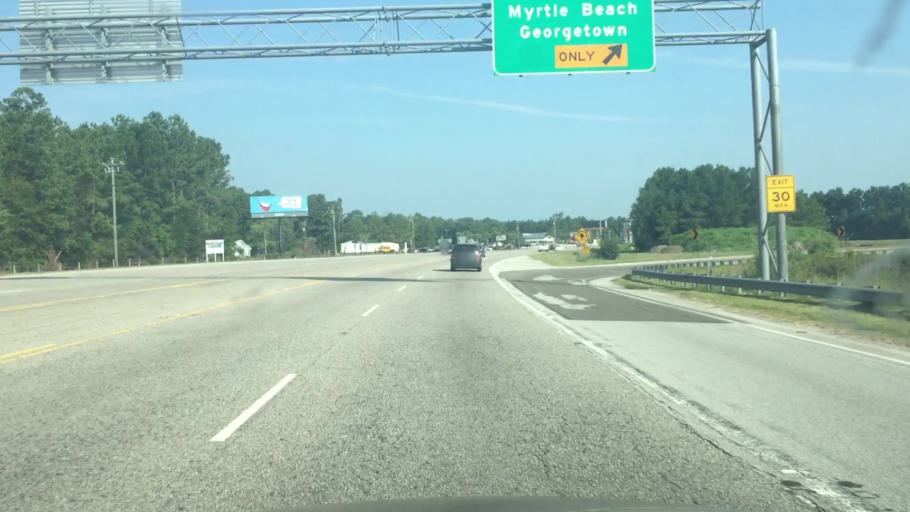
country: US
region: South Carolina
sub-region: Horry County
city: North Myrtle Beach
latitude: 33.8769
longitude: -78.6840
